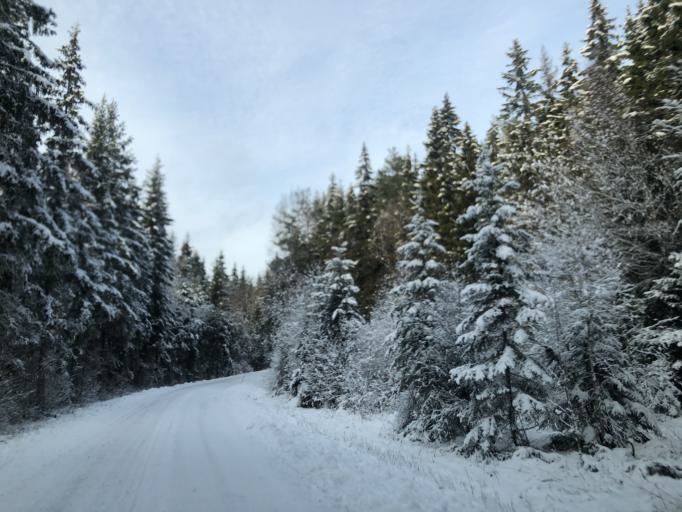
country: SE
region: Vaestra Goetaland
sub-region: Ulricehamns Kommun
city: Ulricehamn
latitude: 57.7754
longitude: 13.5231
